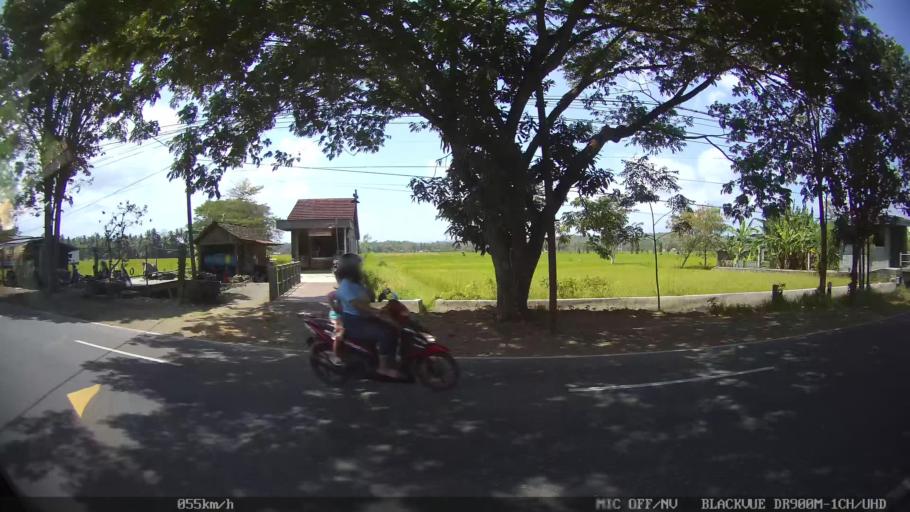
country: ID
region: Daerah Istimewa Yogyakarta
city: Pandak
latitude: -7.9210
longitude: 110.2820
